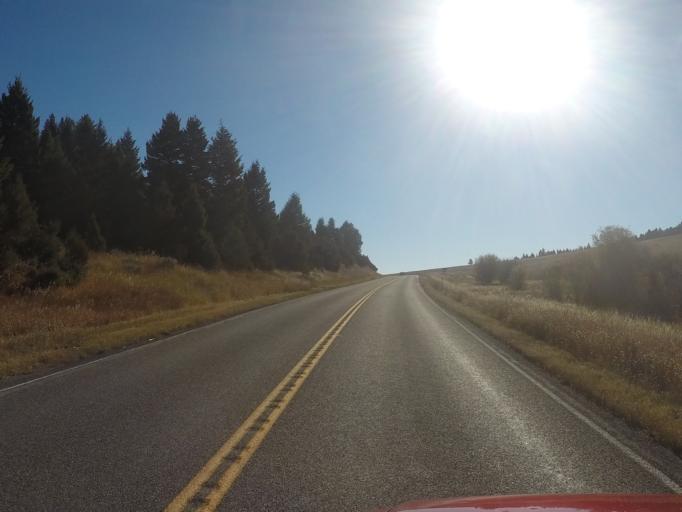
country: US
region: Montana
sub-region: Meagher County
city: White Sulphur Springs
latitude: 46.3568
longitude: -111.0886
